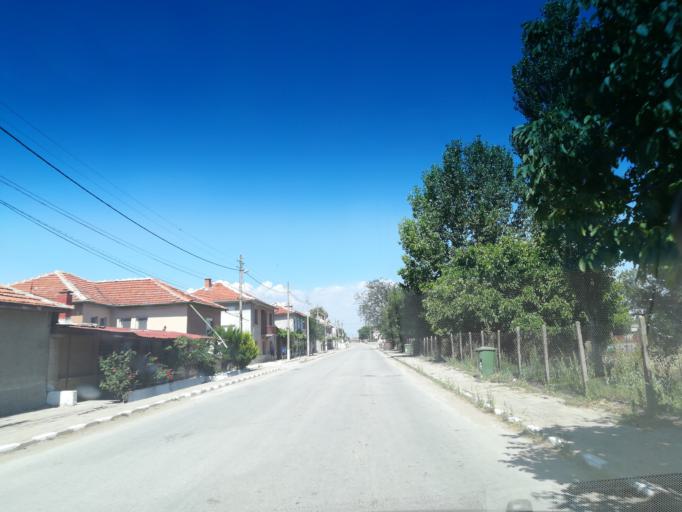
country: BG
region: Plovdiv
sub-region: Obshtina Sadovo
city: Sadovo
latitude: 42.0238
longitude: 25.1032
